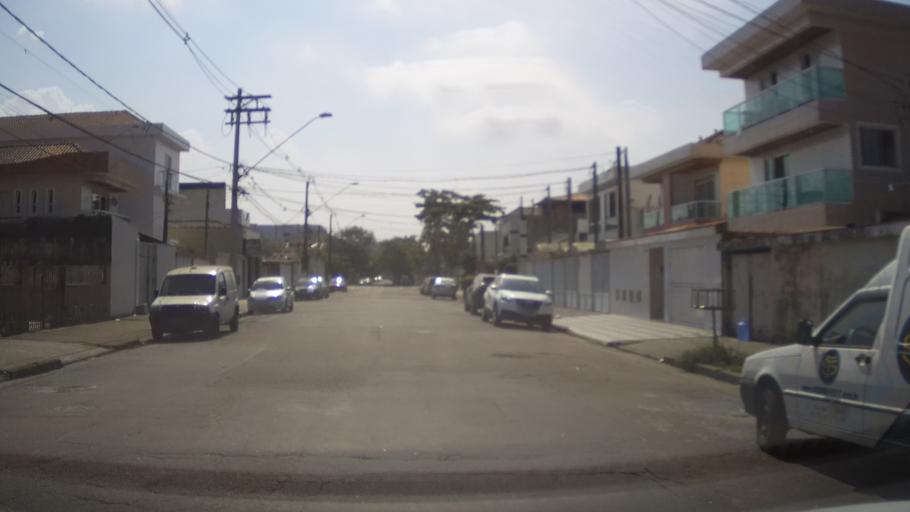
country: BR
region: Sao Paulo
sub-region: Santos
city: Santos
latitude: -23.9755
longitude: -46.2962
